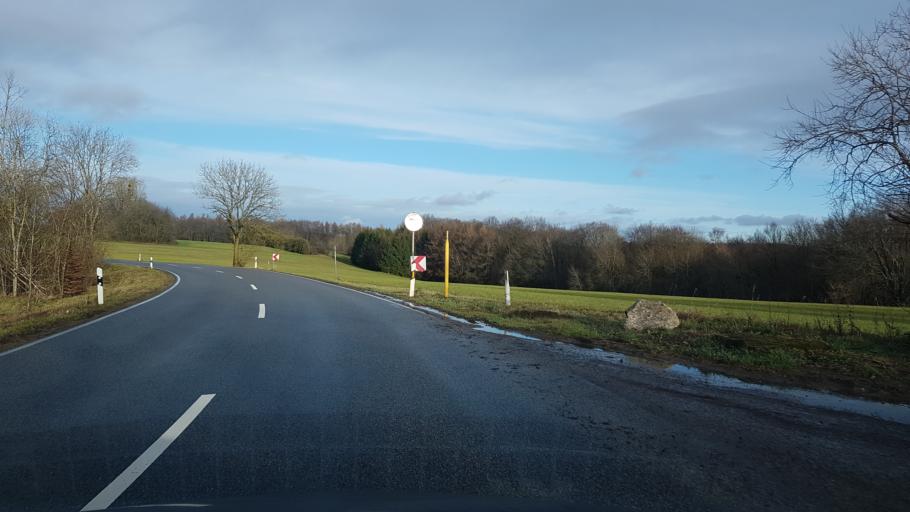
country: DE
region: Saarland
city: Sankt Ingbert
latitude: 49.2401
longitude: 7.1279
